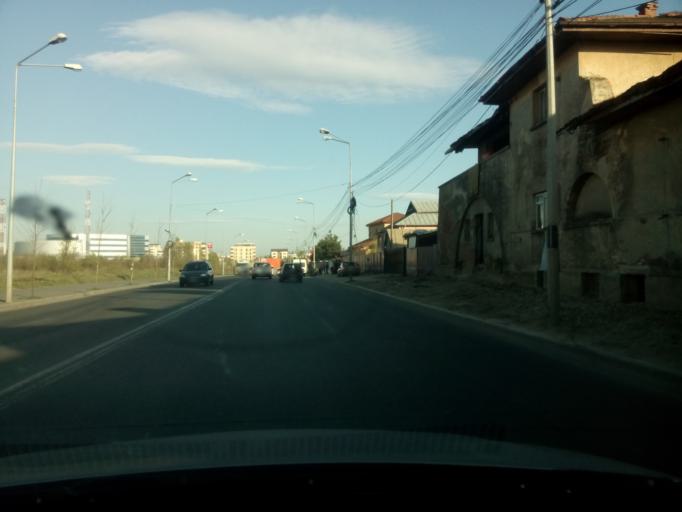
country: RO
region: Ilfov
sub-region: Comuna Otopeni
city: Otopeni
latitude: 44.5016
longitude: 26.0614
